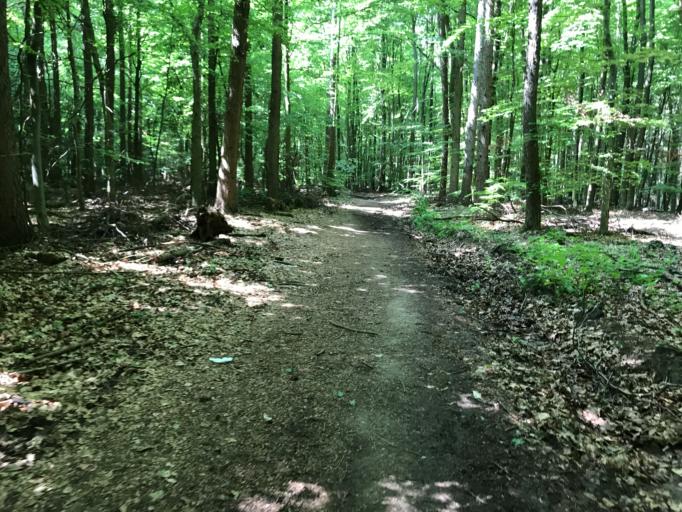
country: DE
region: Hesse
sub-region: Regierungsbezirk Darmstadt
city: Walluf
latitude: 50.0763
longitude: 8.1387
